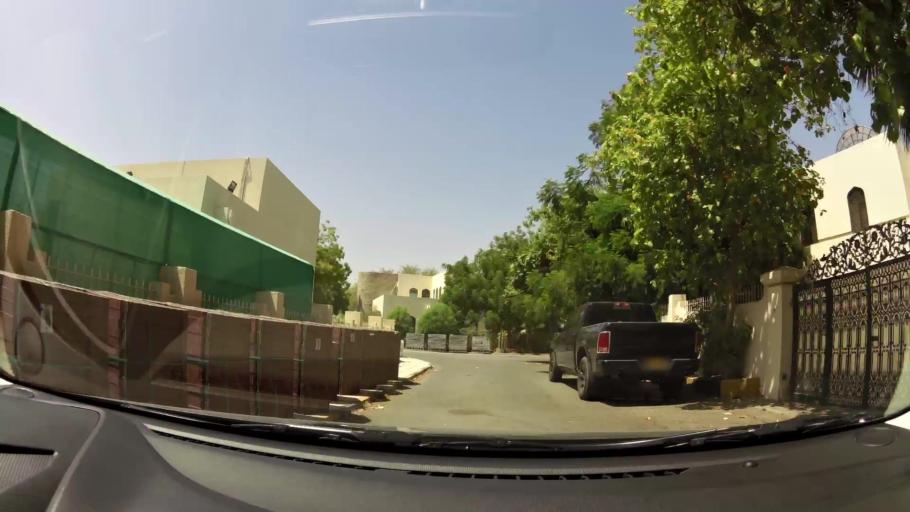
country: OM
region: Muhafazat Masqat
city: Bawshar
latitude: 23.5905
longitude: 58.3983
